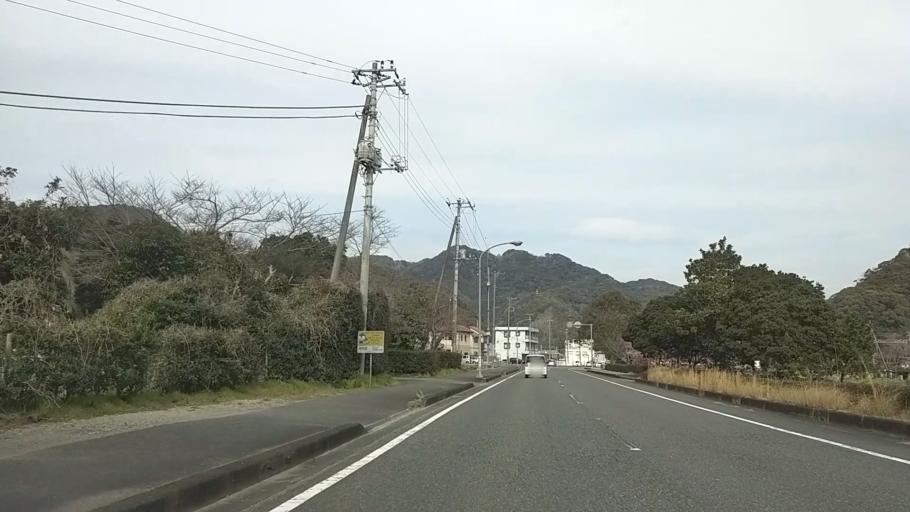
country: JP
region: Shizuoka
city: Shimoda
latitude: 34.6974
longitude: 138.9402
